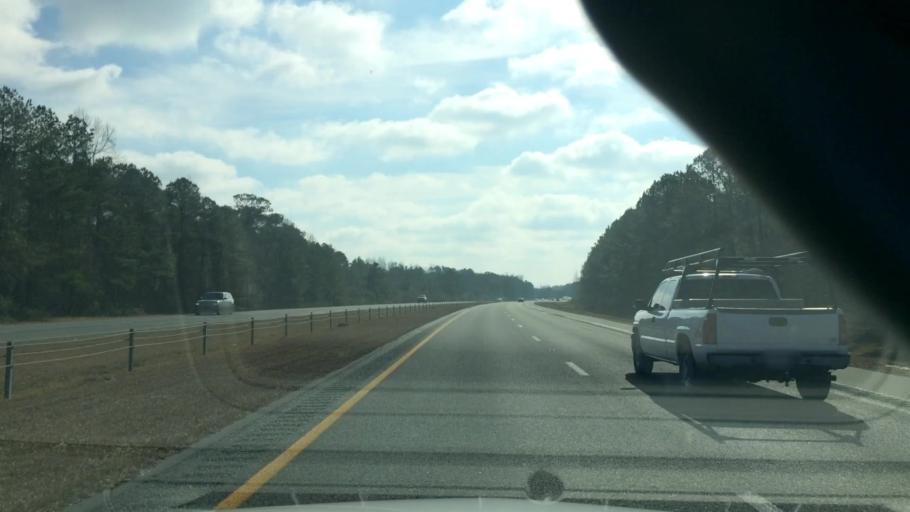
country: US
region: North Carolina
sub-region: Duplin County
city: Wallace
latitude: 34.6987
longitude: -77.9448
